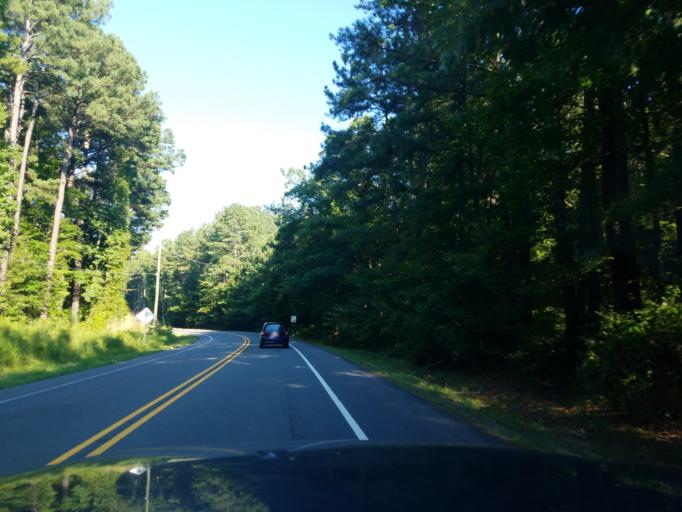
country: US
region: North Carolina
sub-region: Orange County
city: Chapel Hill
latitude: 35.8878
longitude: -78.9814
